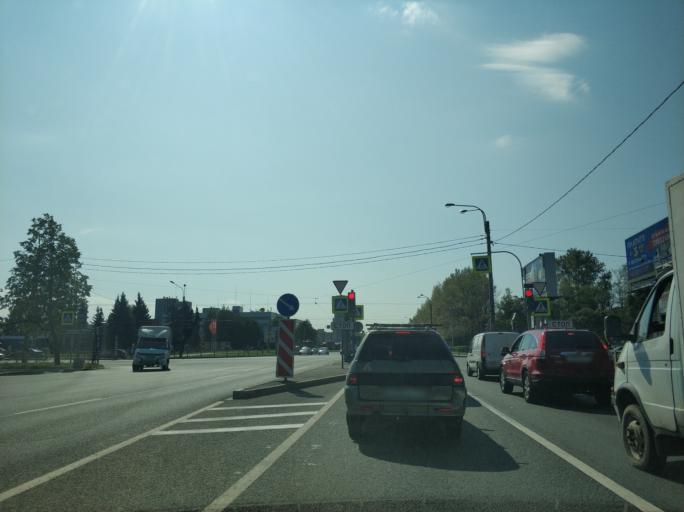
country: RU
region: St.-Petersburg
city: Kupchino
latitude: 59.8530
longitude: 30.3375
